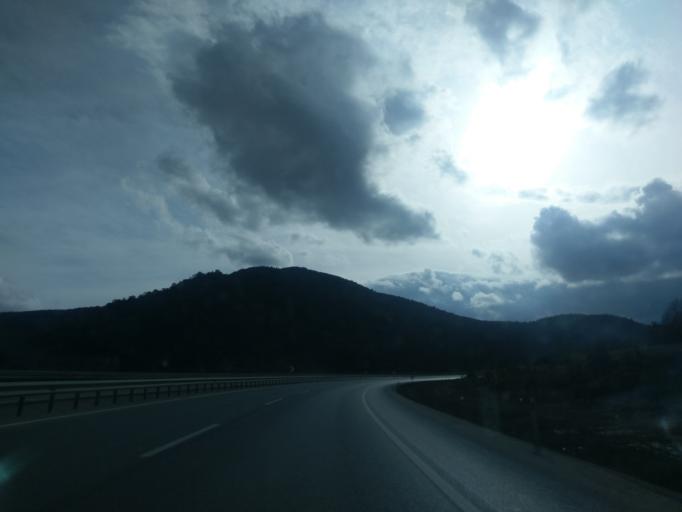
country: TR
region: Kuetahya
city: Sabuncu
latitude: 39.5598
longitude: 30.0766
